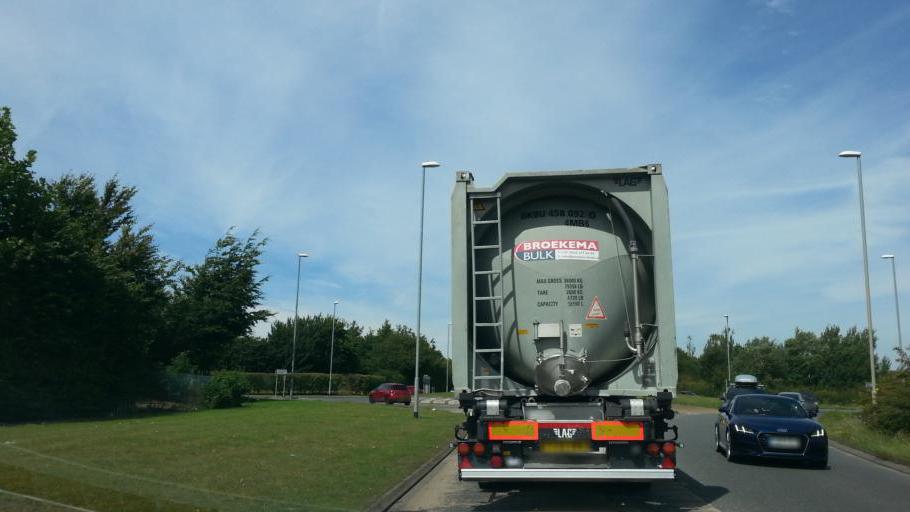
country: GB
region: England
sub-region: Suffolk
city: Exning
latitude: 52.2904
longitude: 0.3916
